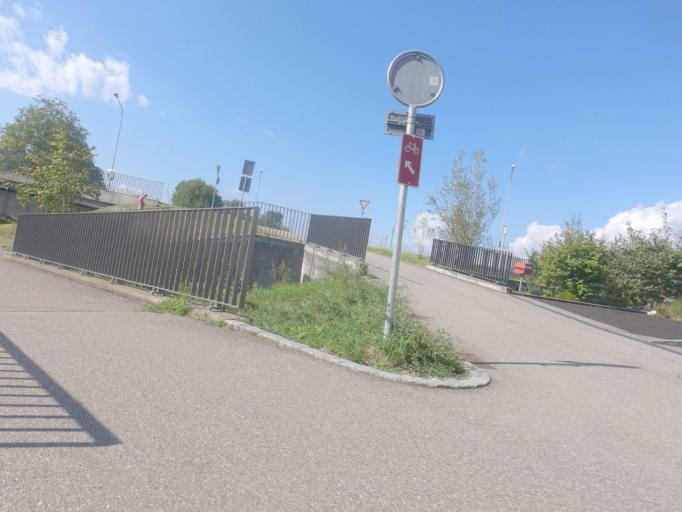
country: CH
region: Solothurn
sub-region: Bezirk Olten
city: Wangen
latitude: 47.3359
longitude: 7.8621
